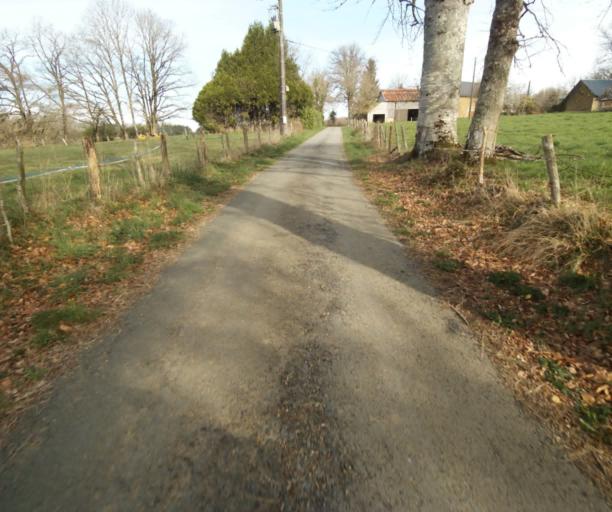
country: FR
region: Limousin
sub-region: Departement de la Correze
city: Chamboulive
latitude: 45.4244
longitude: 1.7602
